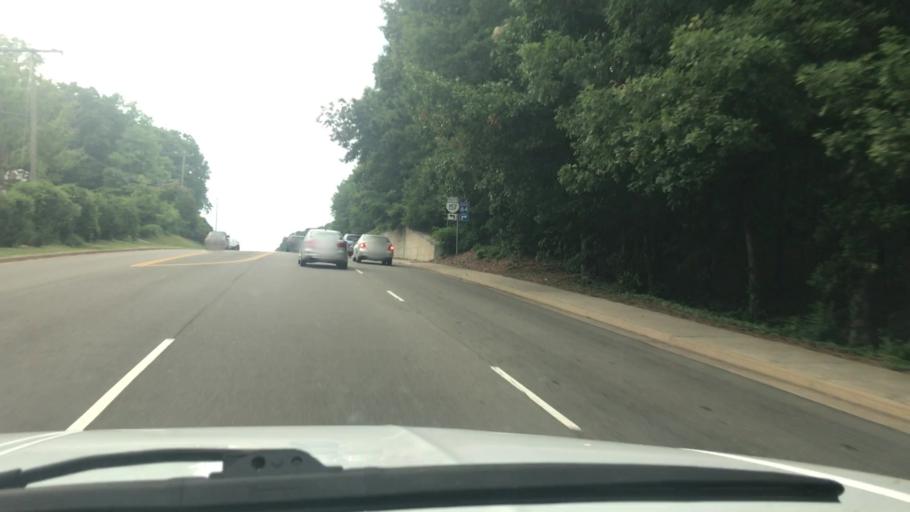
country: US
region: Virginia
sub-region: Henrico County
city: Tuckahoe
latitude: 37.6074
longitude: -77.5872
